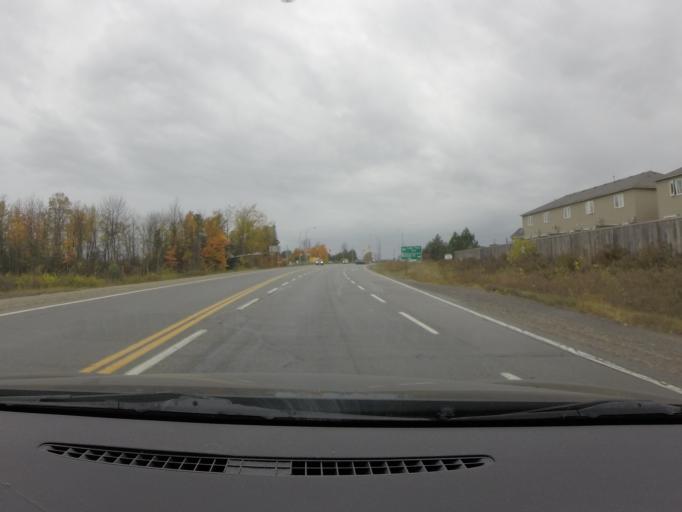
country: CA
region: Ontario
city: Carleton Place
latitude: 45.1230
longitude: -76.1391
